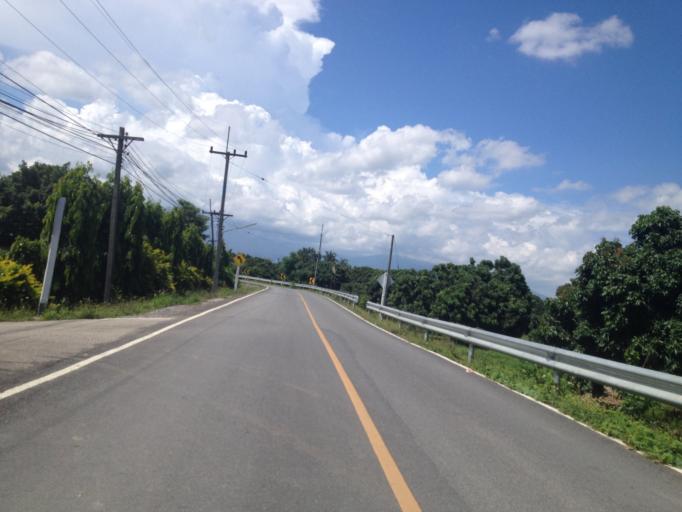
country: TH
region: Chiang Mai
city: Hang Dong
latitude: 18.6582
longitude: 98.9643
